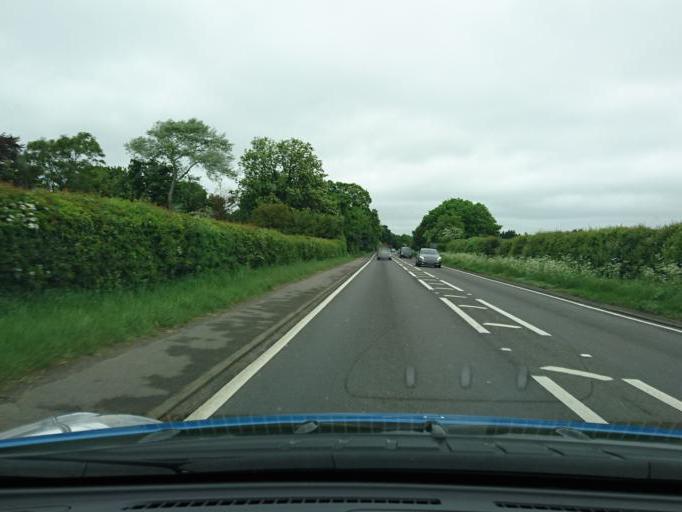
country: GB
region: England
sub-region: Oxfordshire
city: Boars Hill
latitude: 51.7237
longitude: -1.3315
